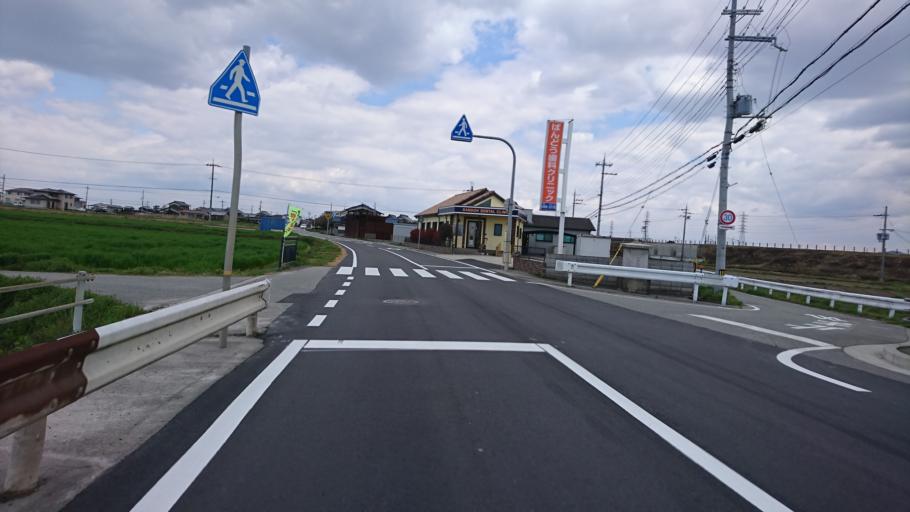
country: JP
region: Hyogo
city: Miki
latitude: 34.7434
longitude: 134.9338
